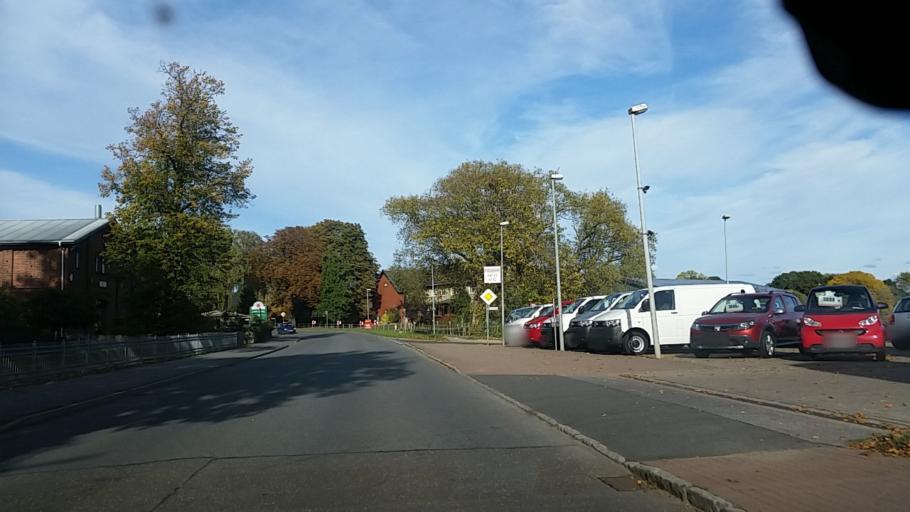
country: DE
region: Schleswig-Holstein
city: Delingsdorf
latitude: 53.7052
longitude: 10.2517
